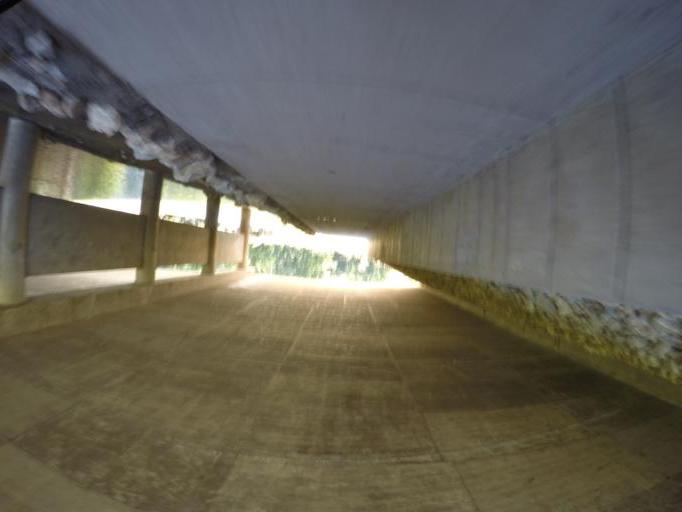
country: US
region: Kansas
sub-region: Johnson County
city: Lenexa
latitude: 38.9312
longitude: -94.6976
